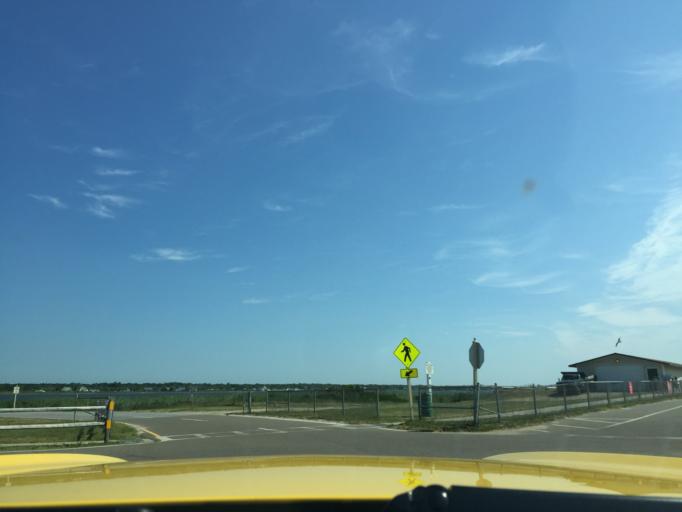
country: US
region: New York
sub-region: Suffolk County
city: Mastic Beach
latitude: 40.7359
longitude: -72.8575
